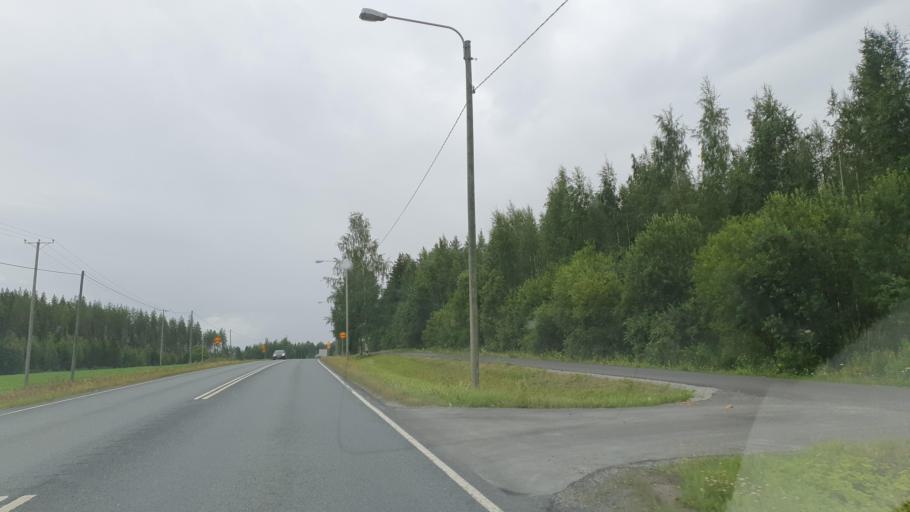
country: FI
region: Northern Savo
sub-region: Kuopio
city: Siilinjaervi
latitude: 63.1329
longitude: 27.6234
